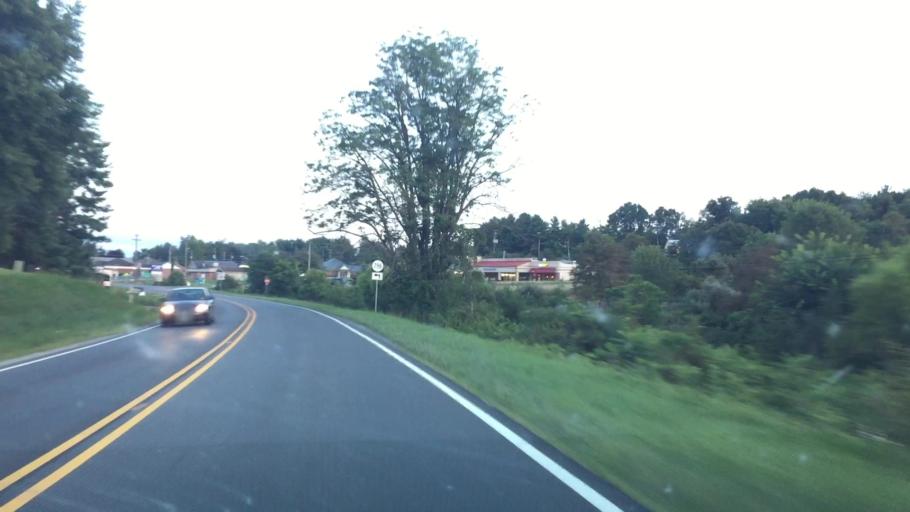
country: US
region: Virginia
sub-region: Wythe County
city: Wytheville
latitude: 36.9325
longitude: -80.9440
